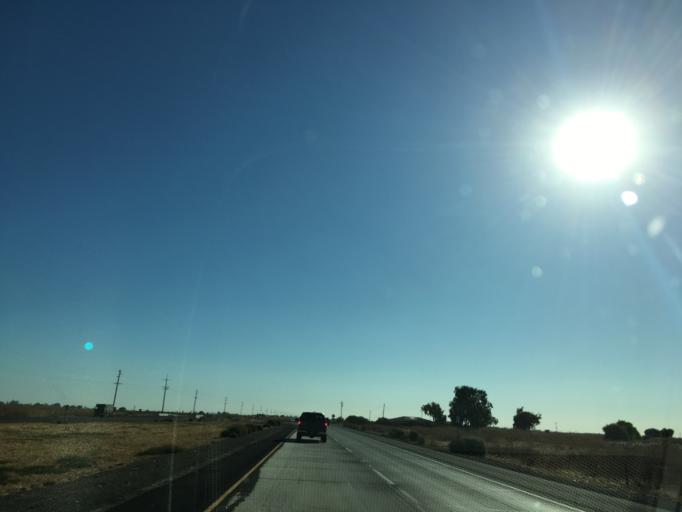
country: US
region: California
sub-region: Merced County
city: Los Banos
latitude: 37.0557
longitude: -120.7904
